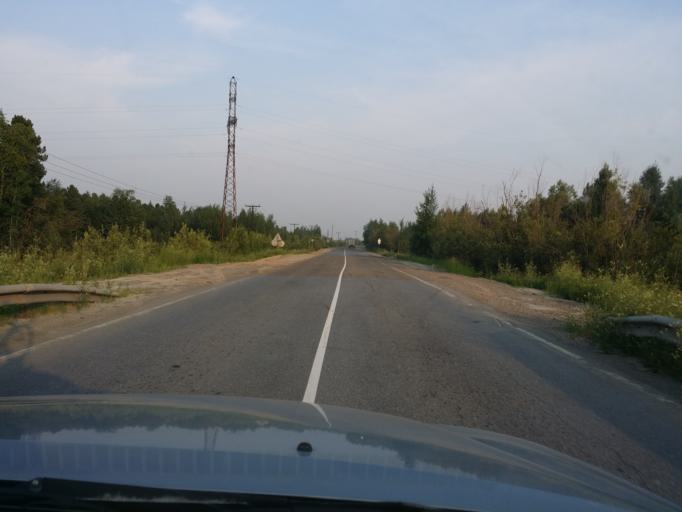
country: RU
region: Khanty-Mansiyskiy Avtonomnyy Okrug
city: Nizhnevartovsk
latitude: 61.1951
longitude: 76.5499
